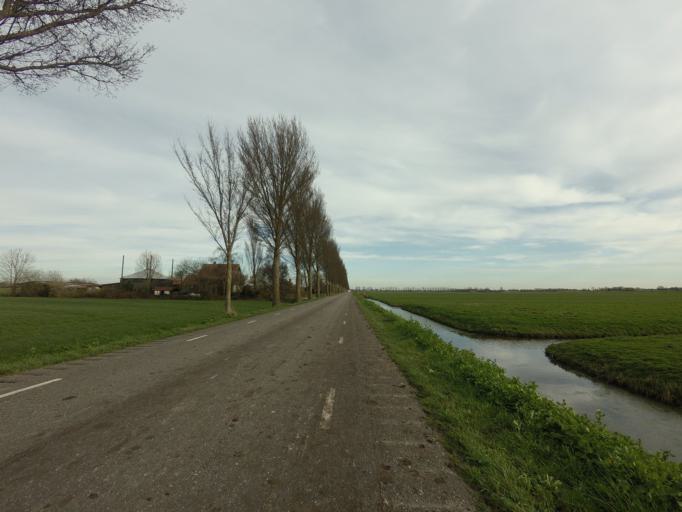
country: NL
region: Utrecht
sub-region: Gemeente De Ronde Venen
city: Mijdrecht
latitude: 52.2002
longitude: 4.8314
